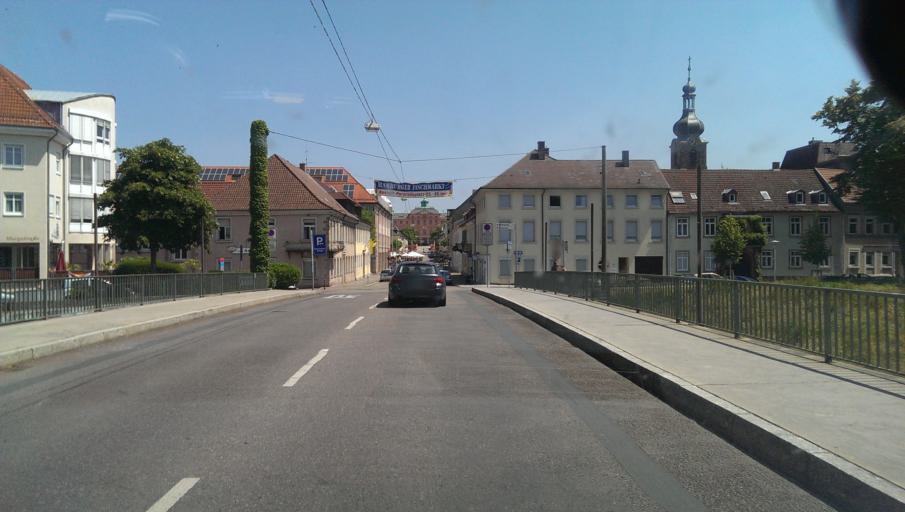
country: DE
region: Baden-Wuerttemberg
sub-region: Karlsruhe Region
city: Rastatt
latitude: 48.8569
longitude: 8.2005
